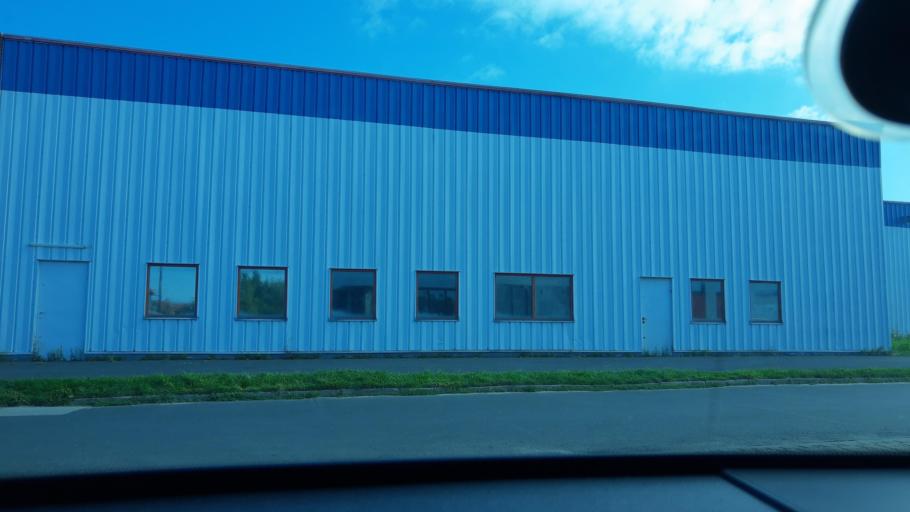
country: PL
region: Lodz Voivodeship
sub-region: Powiat sieradzki
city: Sieradz
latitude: 51.5826
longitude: 18.7195
